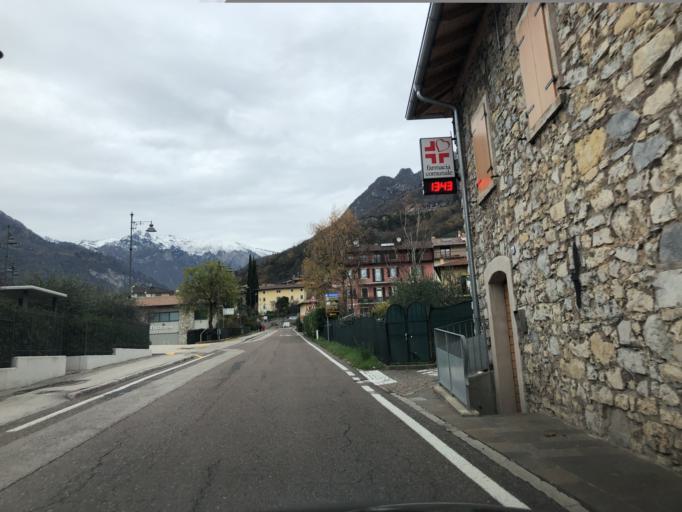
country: IT
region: Trentino-Alto Adige
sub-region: Provincia di Trento
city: Tenno
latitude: 45.9181
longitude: 10.8329
